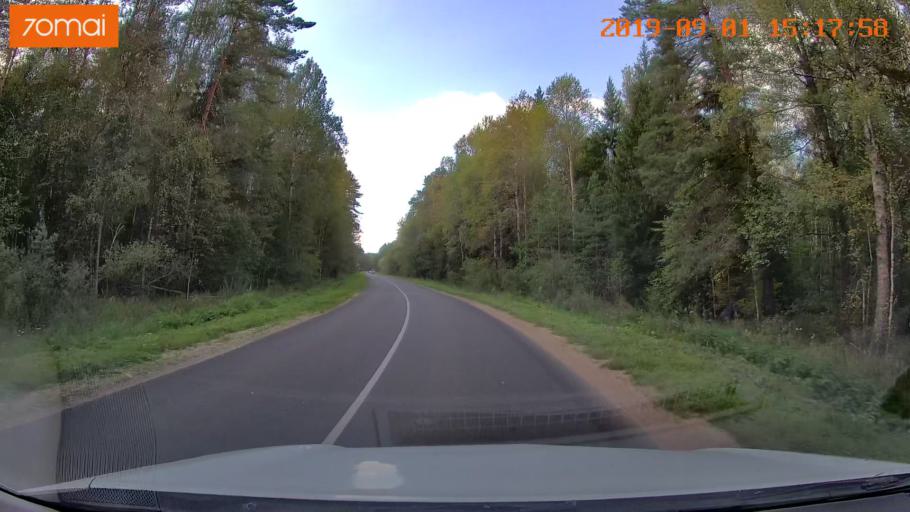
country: RU
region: Kaluga
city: Maloyaroslavets
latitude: 54.9036
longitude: 36.5161
